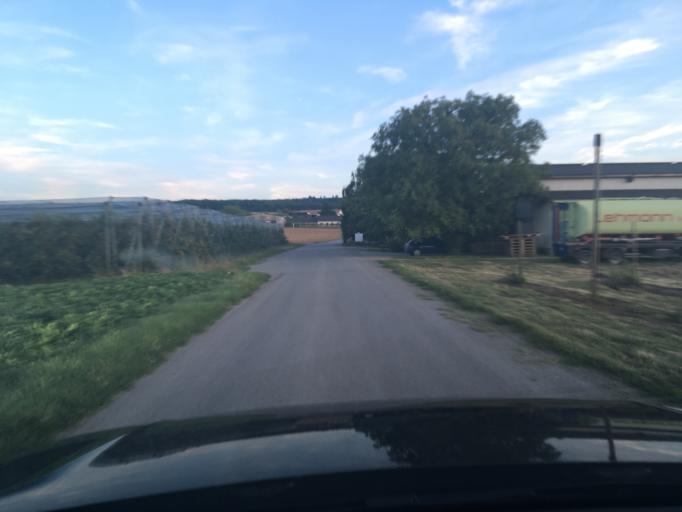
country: DE
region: Baden-Wuerttemberg
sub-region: Regierungsbezirk Stuttgart
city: Schwaigern
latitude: 49.1349
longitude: 9.0483
